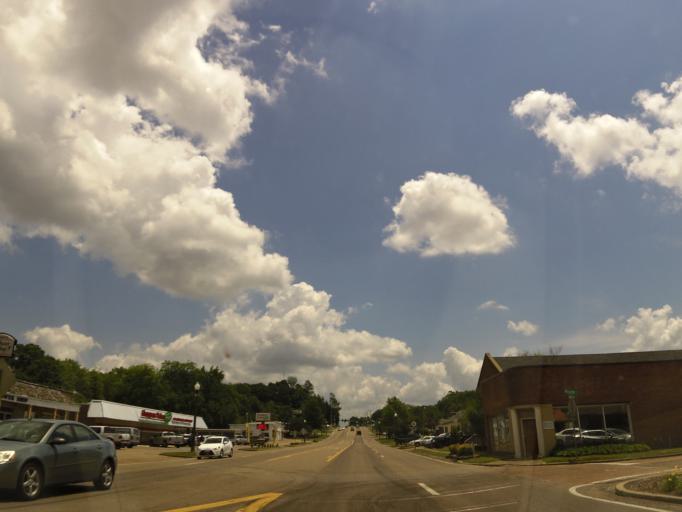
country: US
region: Mississippi
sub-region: Lee County
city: Tupelo
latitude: 34.2577
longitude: -88.6824
